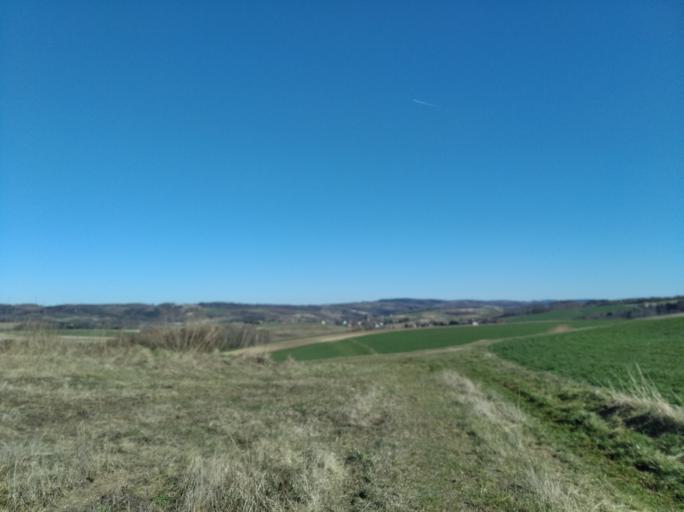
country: PL
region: Subcarpathian Voivodeship
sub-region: Powiat strzyzowski
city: Wisniowa
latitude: 49.9142
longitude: 21.6850
